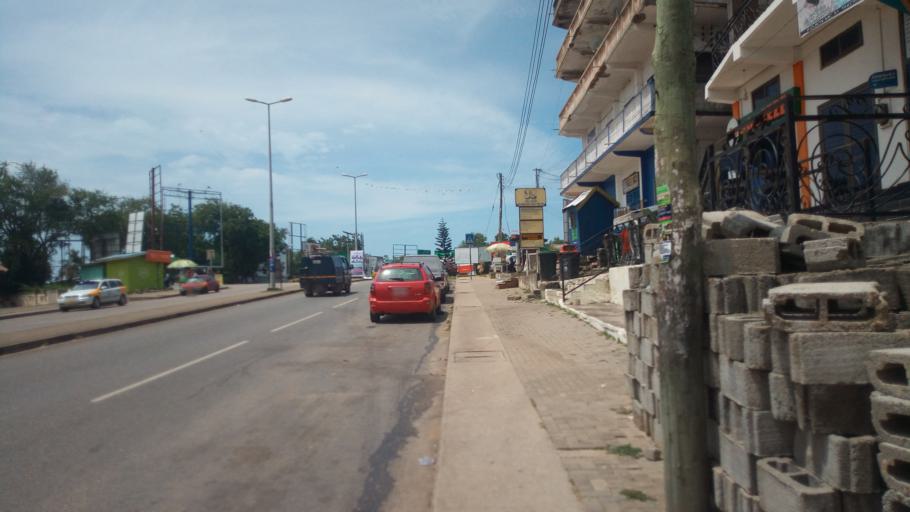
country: GH
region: Western
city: Takoradi
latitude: 4.8935
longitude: -1.7529
